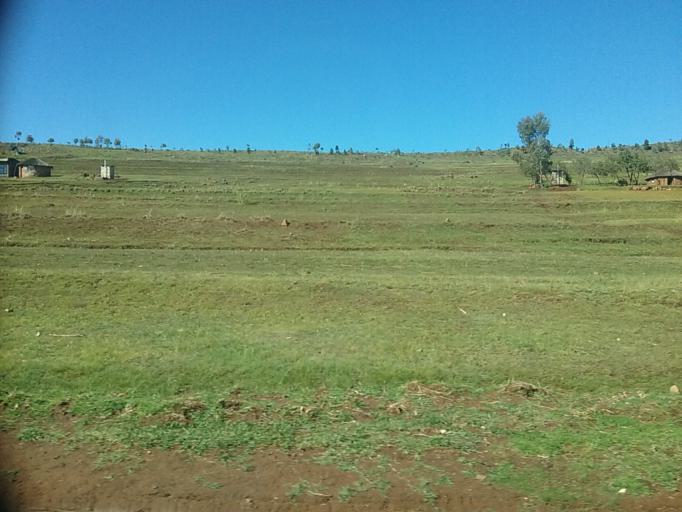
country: LS
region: Berea
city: Teyateyaneng
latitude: -29.2315
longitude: 27.8871
